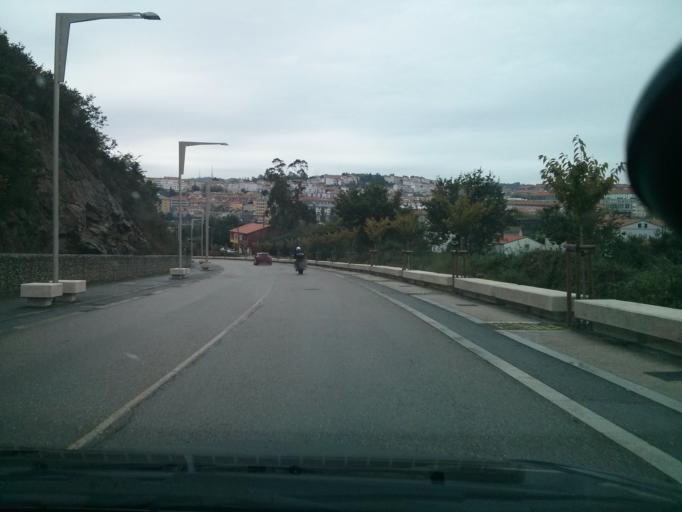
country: ES
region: Galicia
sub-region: Provincia da Coruna
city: Santiago de Compostela
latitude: 42.8759
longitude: -8.5254
